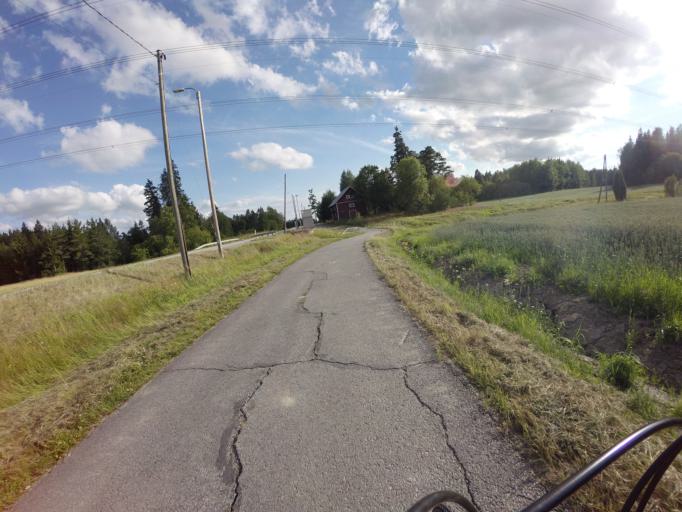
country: FI
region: Varsinais-Suomi
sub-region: Turku
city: Vahto
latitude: 60.5809
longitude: 22.3519
